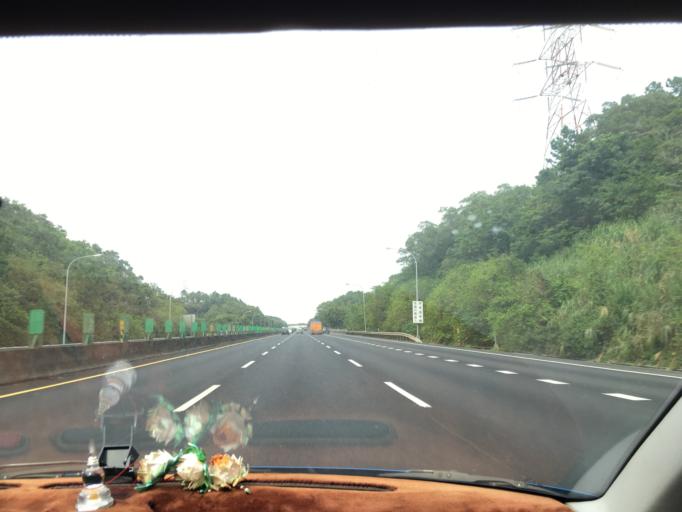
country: TW
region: Taiwan
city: Daxi
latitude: 24.8202
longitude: 121.2002
